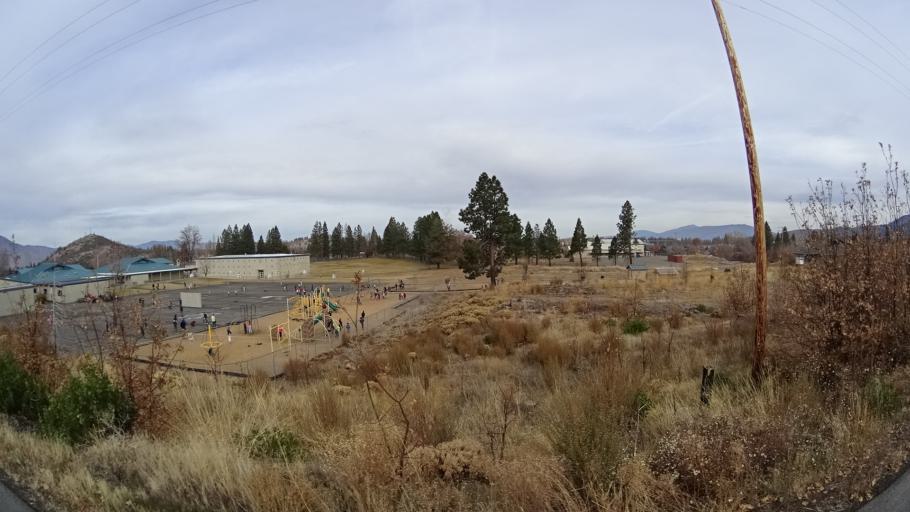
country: US
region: California
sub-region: Siskiyou County
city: Weed
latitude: 41.4270
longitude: -122.3789
